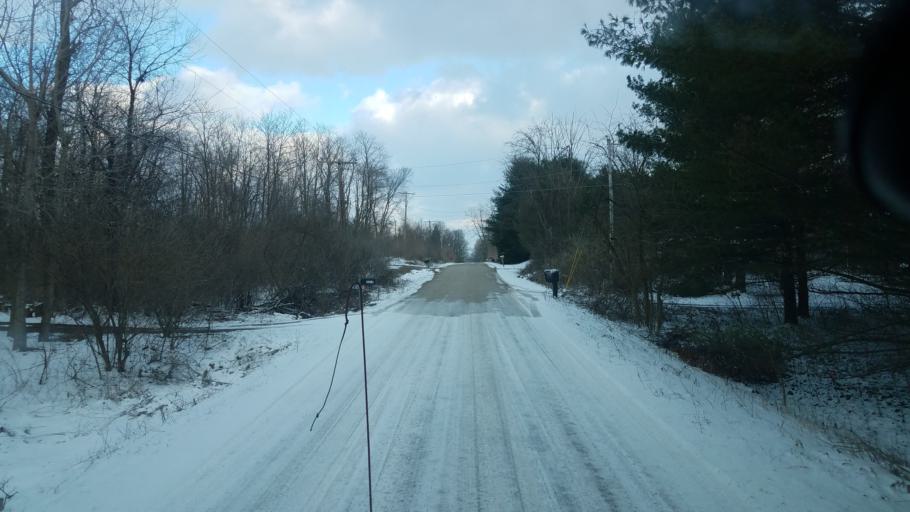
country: US
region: Ohio
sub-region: Delaware County
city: Ashley
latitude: 40.3953
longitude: -82.8691
